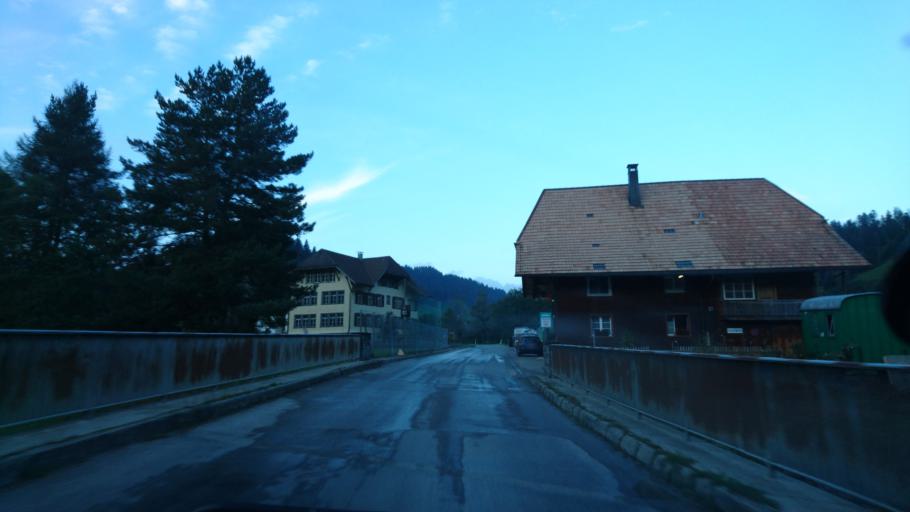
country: CH
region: Bern
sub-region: Emmental District
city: Trub
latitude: 46.9497
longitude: 7.8902
